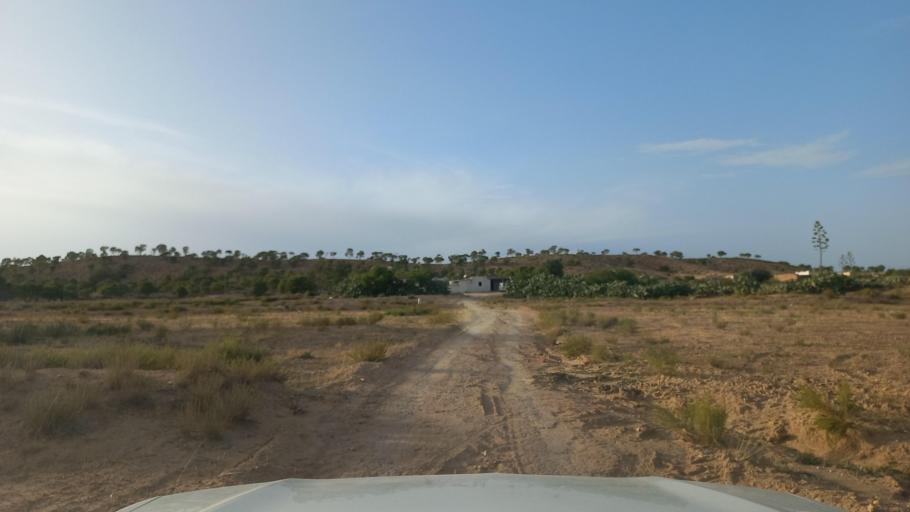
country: TN
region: Al Qasrayn
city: Sbiba
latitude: 35.4036
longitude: 8.8962
